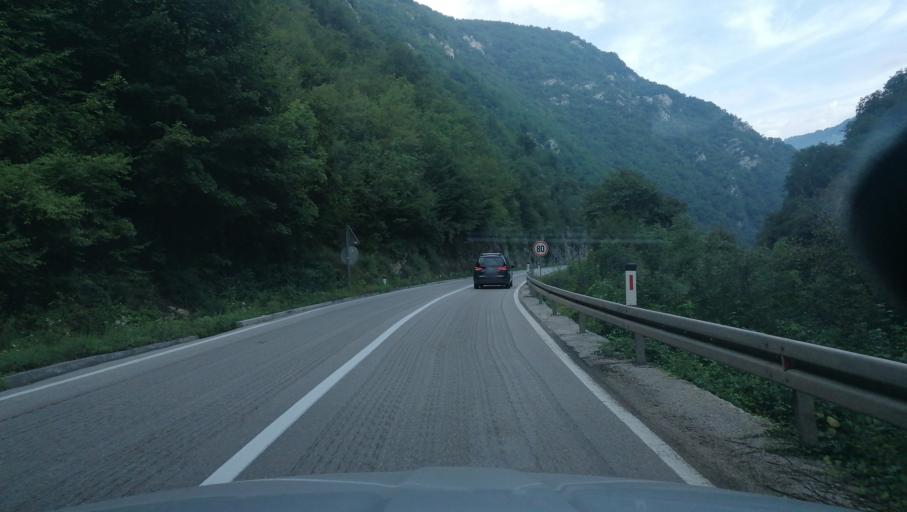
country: BA
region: Federation of Bosnia and Herzegovina
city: Jajce
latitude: 44.4360
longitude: 17.2349
